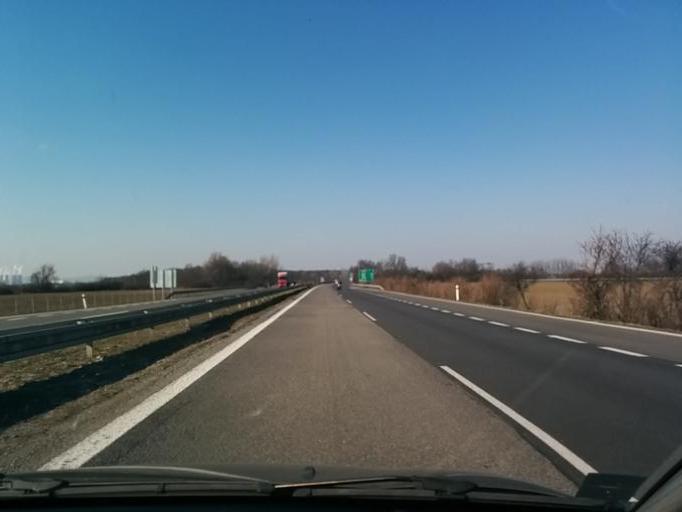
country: SK
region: Trnavsky
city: Leopoldov
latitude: 48.4410
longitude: 17.7396
